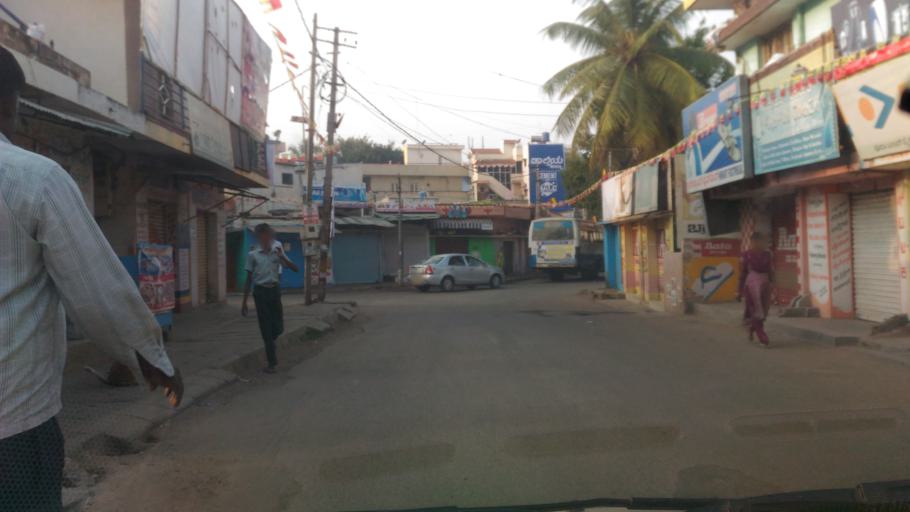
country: IN
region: Karnataka
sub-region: Bangalore Urban
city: Yelahanka
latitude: 13.0428
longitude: 77.5733
